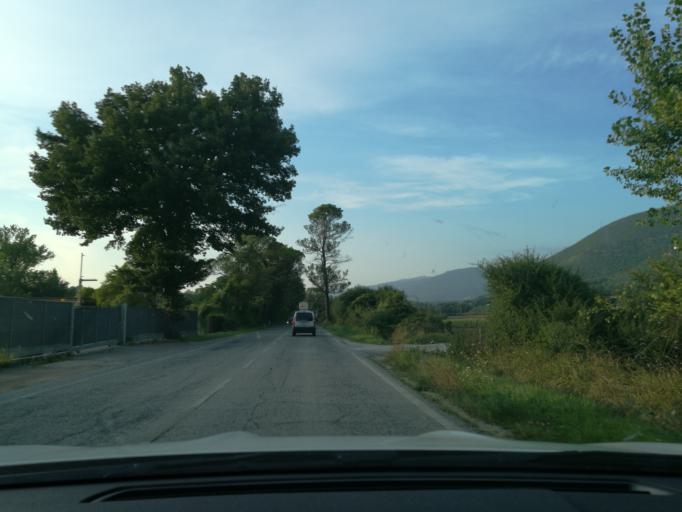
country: IT
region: Umbria
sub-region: Provincia di Terni
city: Acquasparta
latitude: 42.6758
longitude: 12.5515
